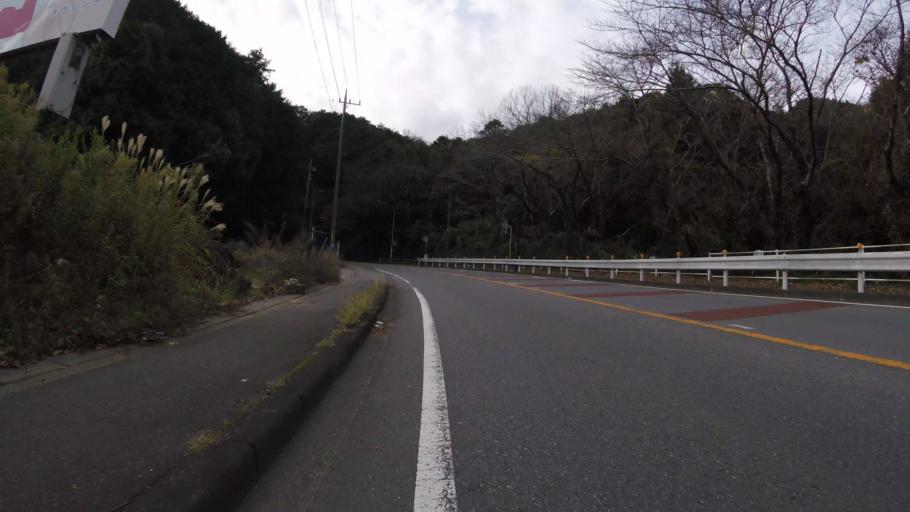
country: JP
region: Shizuoka
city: Numazu
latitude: 35.0831
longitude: 138.8897
